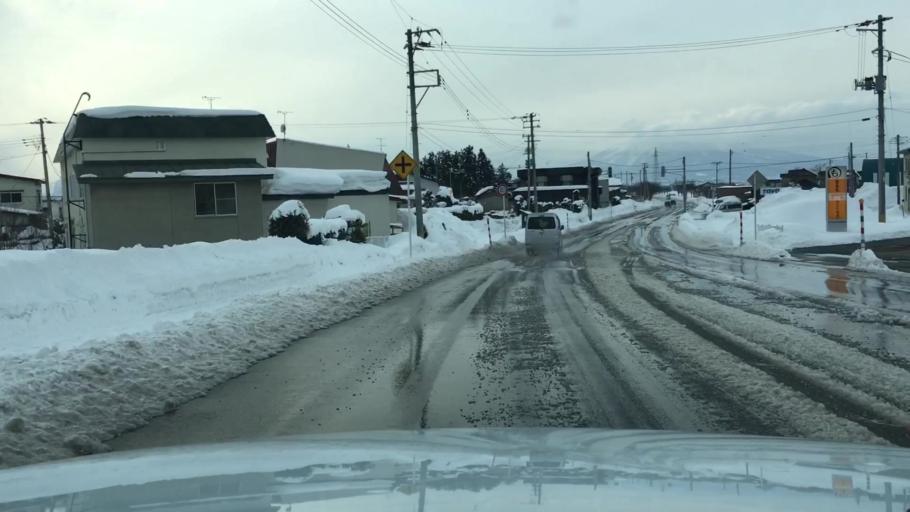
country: JP
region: Aomori
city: Kuroishi
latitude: 40.5912
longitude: 140.5562
